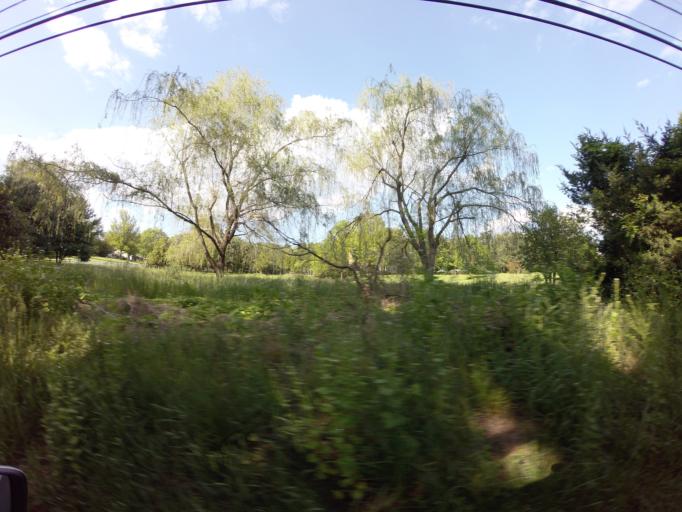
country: US
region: Maryland
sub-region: Baltimore County
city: Hunt Valley
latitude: 39.5036
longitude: -76.6954
